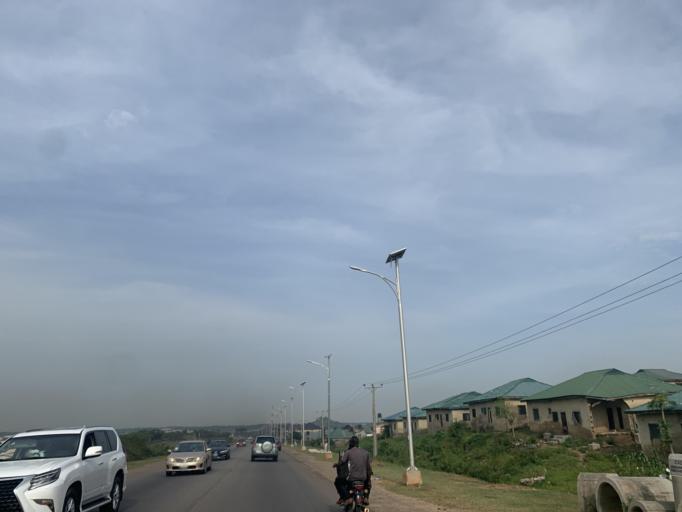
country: NG
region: Abuja Federal Capital Territory
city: Abuja
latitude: 9.0402
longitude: 7.3983
